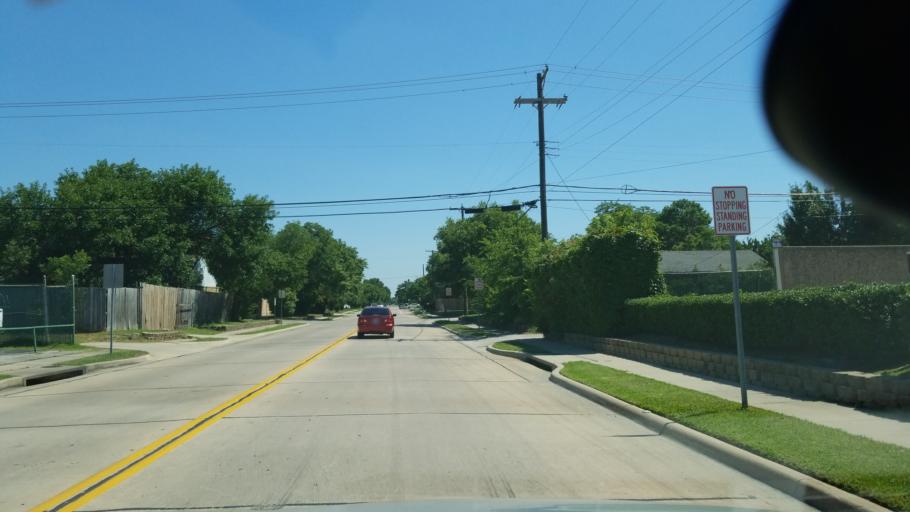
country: US
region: Texas
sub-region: Dallas County
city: Irving
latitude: 32.8358
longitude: -96.9354
